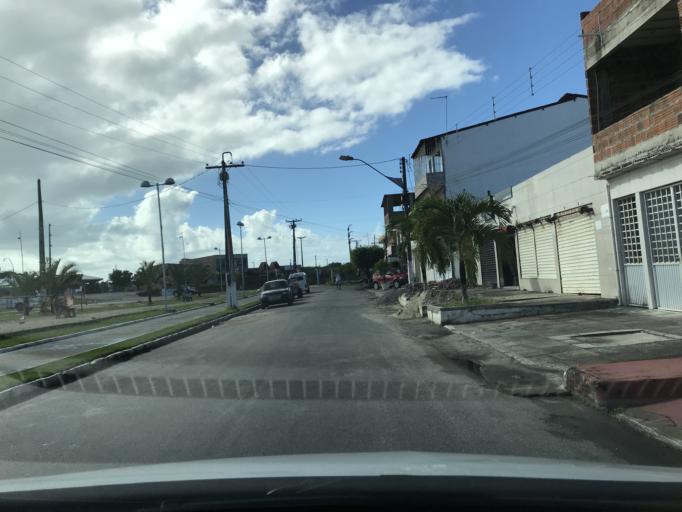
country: BR
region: Pernambuco
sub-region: Ipojuca
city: Ipojuca
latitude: -8.4393
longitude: -35.0120
